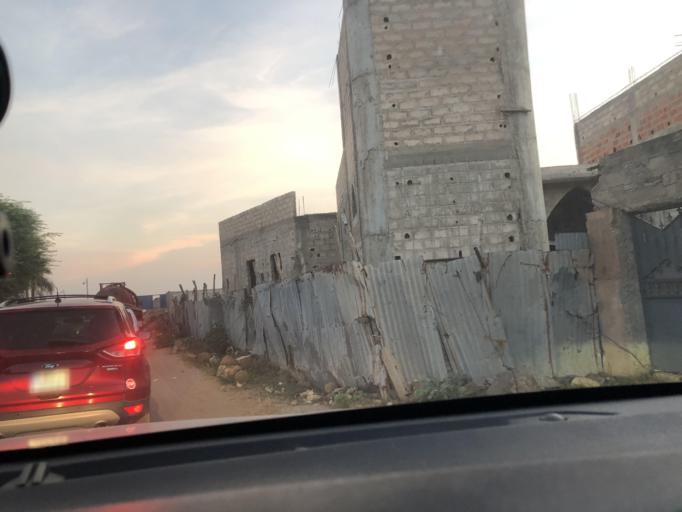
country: SN
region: Dakar
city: Mermoz Boabab
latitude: 14.7367
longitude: -17.5129
